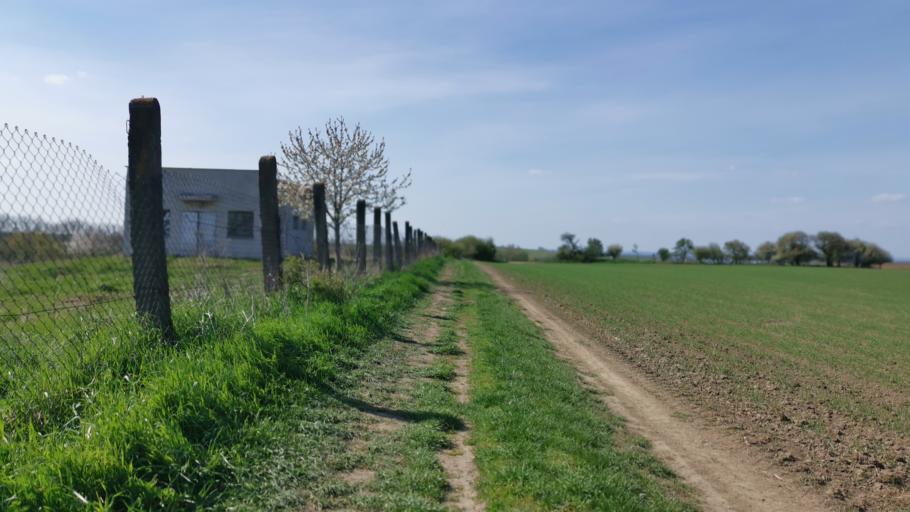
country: SK
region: Trnavsky
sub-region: Okres Skalica
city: Holic
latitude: 48.7678
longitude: 17.1909
